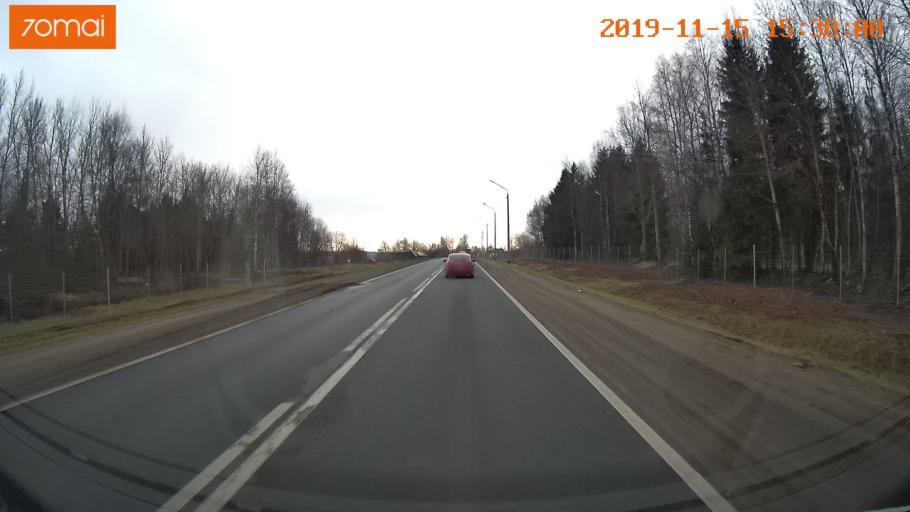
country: RU
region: Jaroslavl
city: Danilov
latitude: 58.0337
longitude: 40.0846
